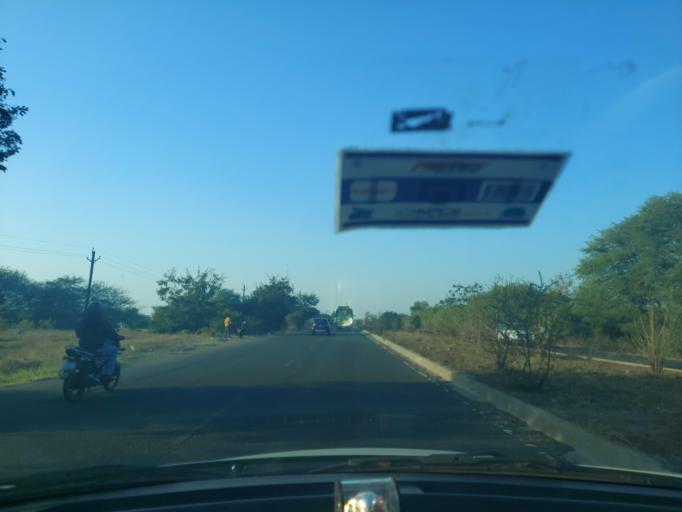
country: IN
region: Madhya Pradesh
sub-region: Indore
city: Sanwer
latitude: 23.0205
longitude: 75.8326
